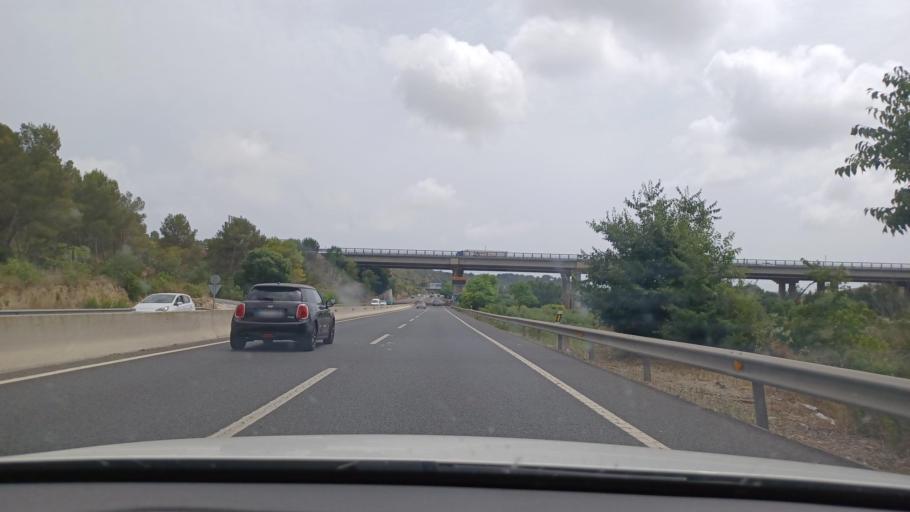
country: ES
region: Catalonia
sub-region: Provincia de Tarragona
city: Constanti
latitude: 41.1474
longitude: 1.2396
